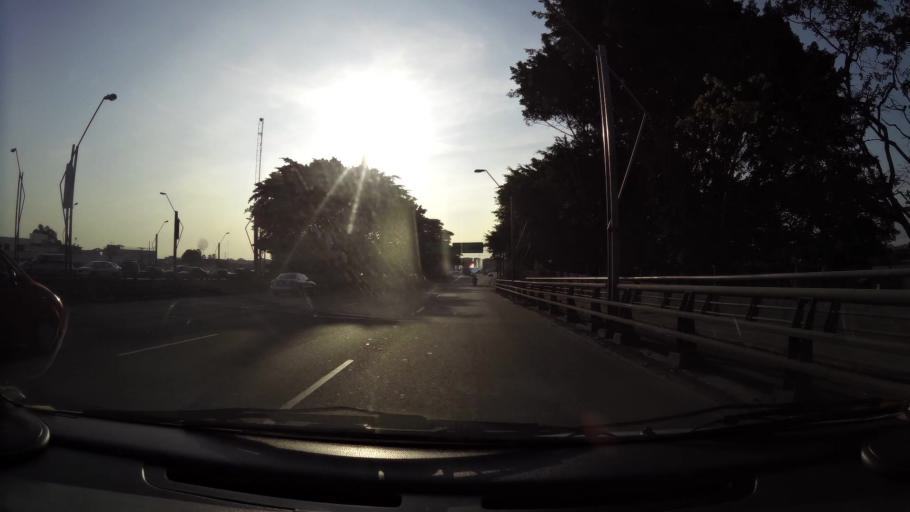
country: EC
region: Guayas
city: Eloy Alfaro
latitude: -2.1528
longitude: -79.8693
